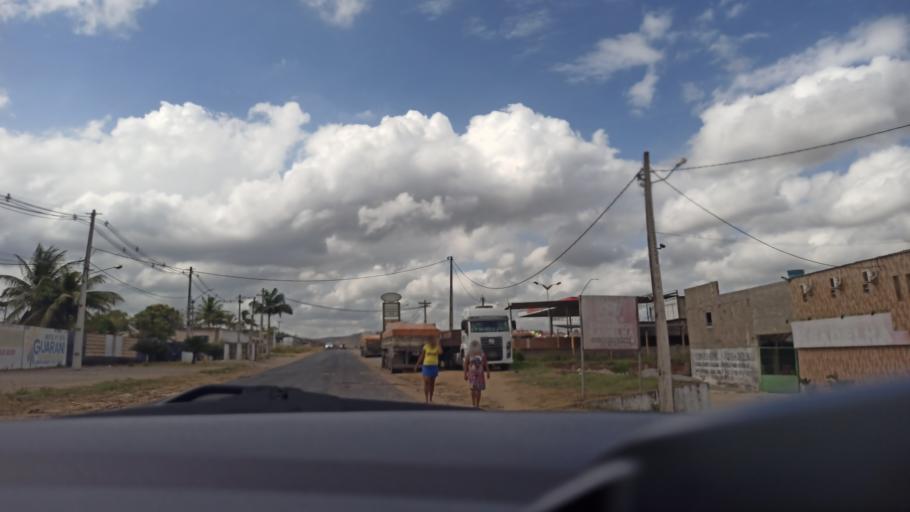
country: BR
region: Pernambuco
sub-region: Timbauba
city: Timbauba
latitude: -7.4948
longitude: -35.2974
